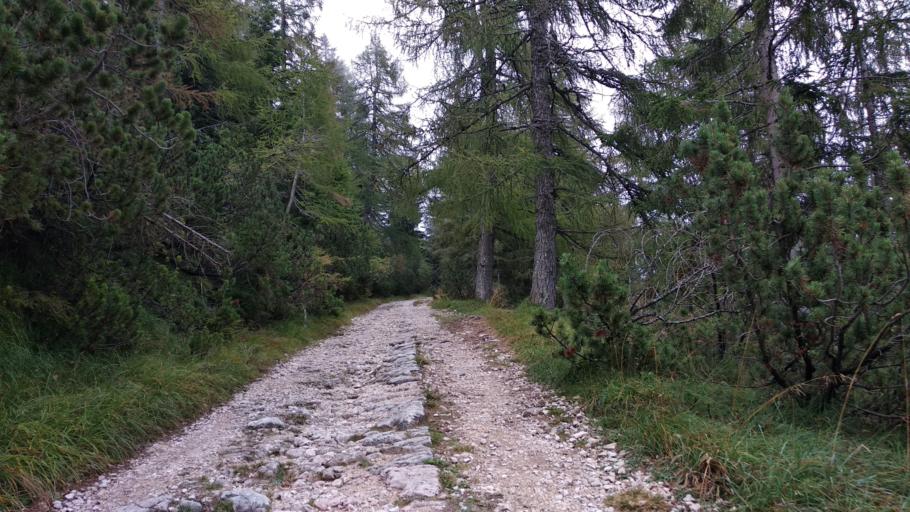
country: IT
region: Veneto
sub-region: Provincia di Vicenza
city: Roana
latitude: 45.9629
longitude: 11.4412
